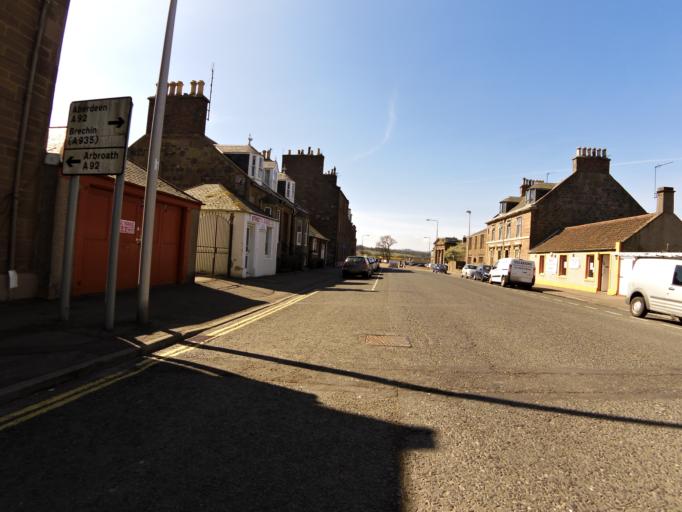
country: GB
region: Scotland
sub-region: Angus
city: Montrose
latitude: 56.7084
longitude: -2.4726
